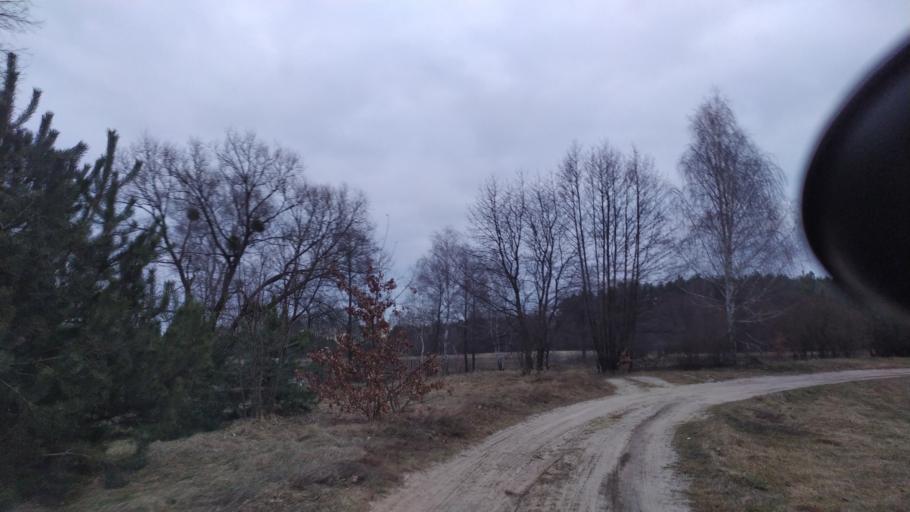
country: PL
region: Lublin Voivodeship
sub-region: Powiat lubartowski
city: Abramow
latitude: 51.4257
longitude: 22.2887
